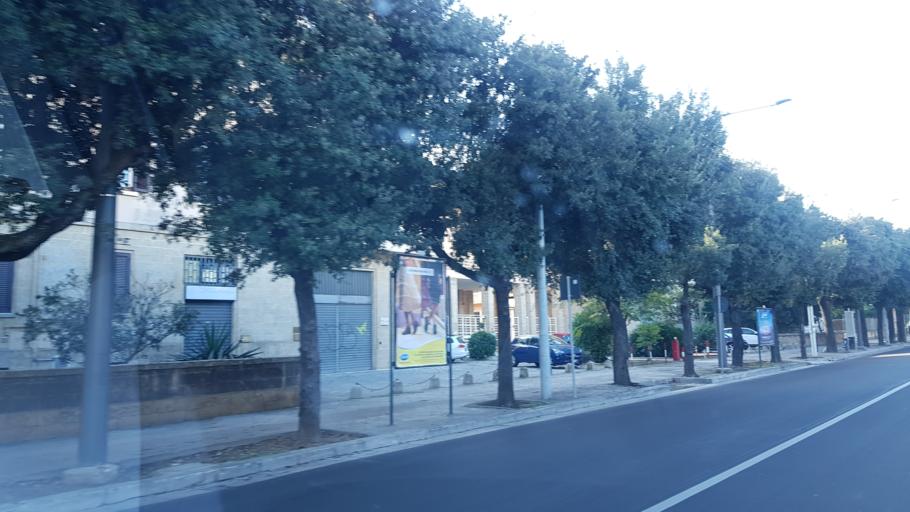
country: IT
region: Apulia
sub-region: Provincia di Lecce
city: Lecce
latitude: 40.3490
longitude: 18.1662
